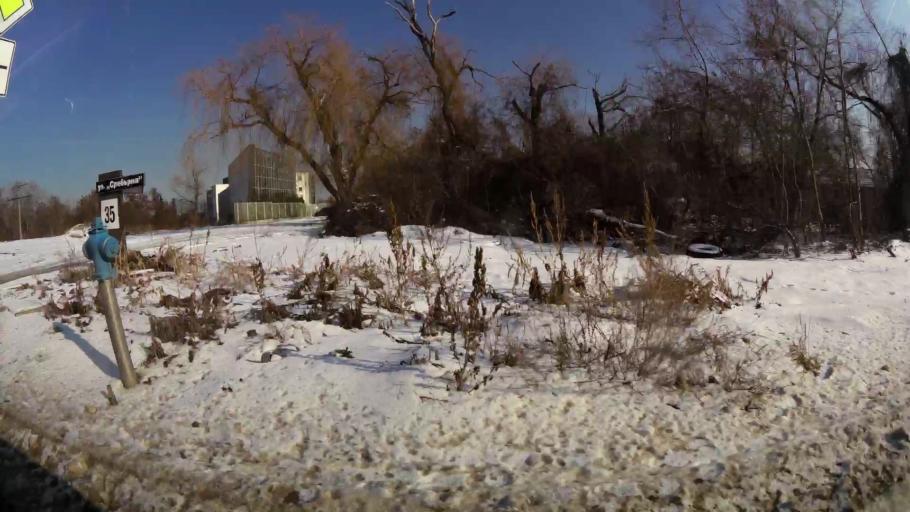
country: BG
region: Sofia-Capital
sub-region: Stolichna Obshtina
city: Sofia
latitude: 42.6566
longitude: 23.3280
